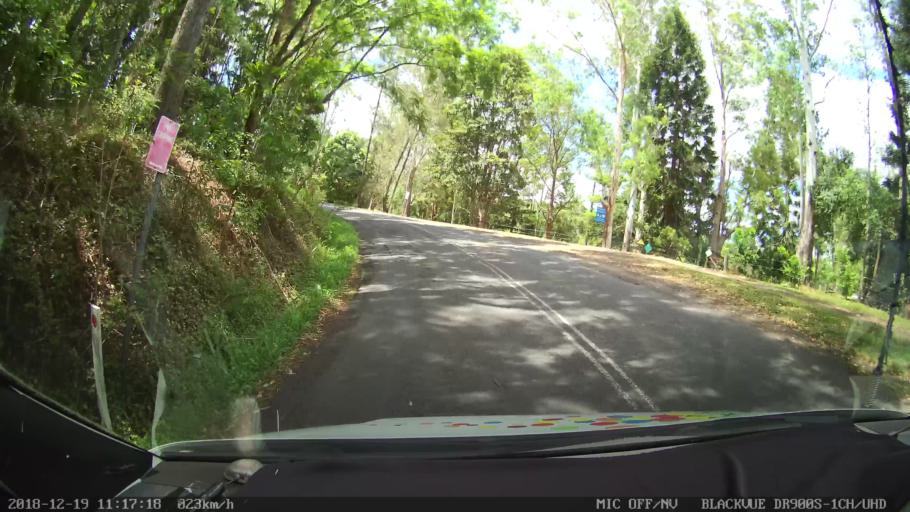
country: AU
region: New South Wales
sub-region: Lismore Municipality
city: Nimbin
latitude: -28.6781
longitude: 153.2796
